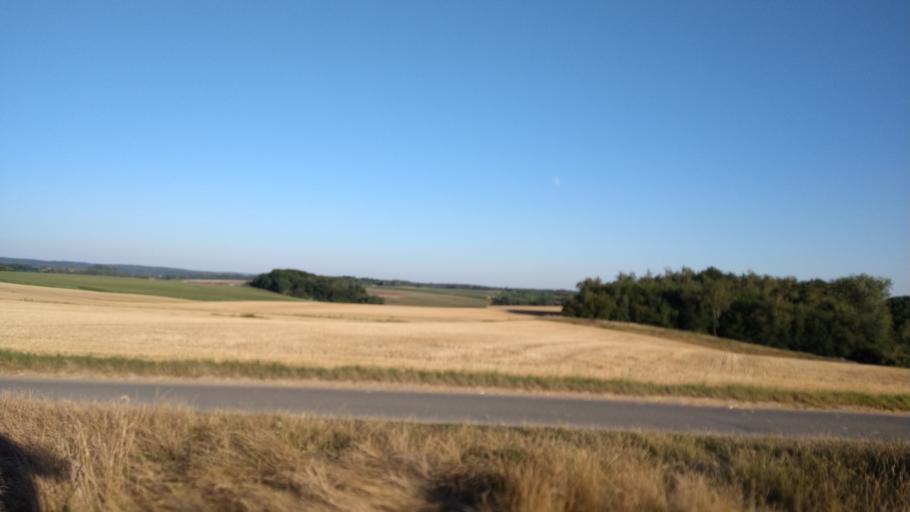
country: BE
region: Flanders
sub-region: Provincie Vlaams-Brabant
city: Huldenberg
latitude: 50.8246
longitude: 4.5754
